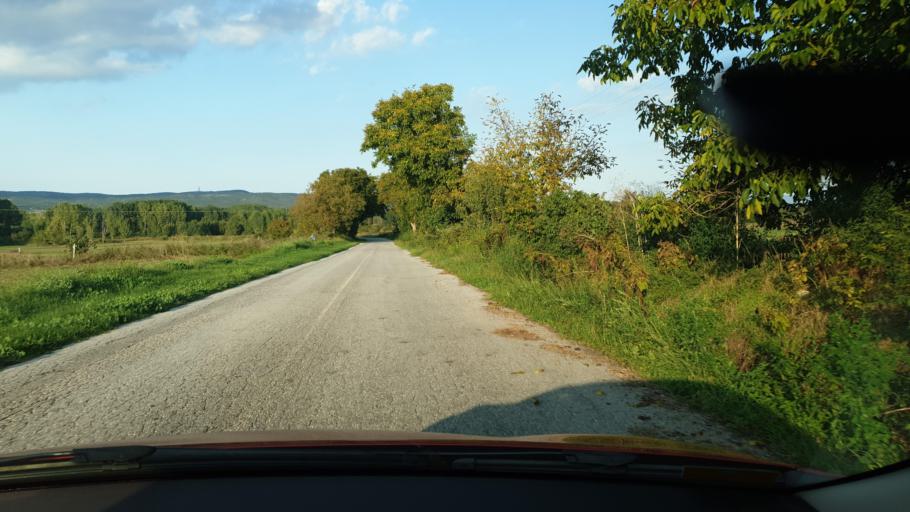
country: GR
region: Central Macedonia
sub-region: Nomos Chalkidikis
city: Galatista
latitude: 40.5574
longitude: 23.3055
